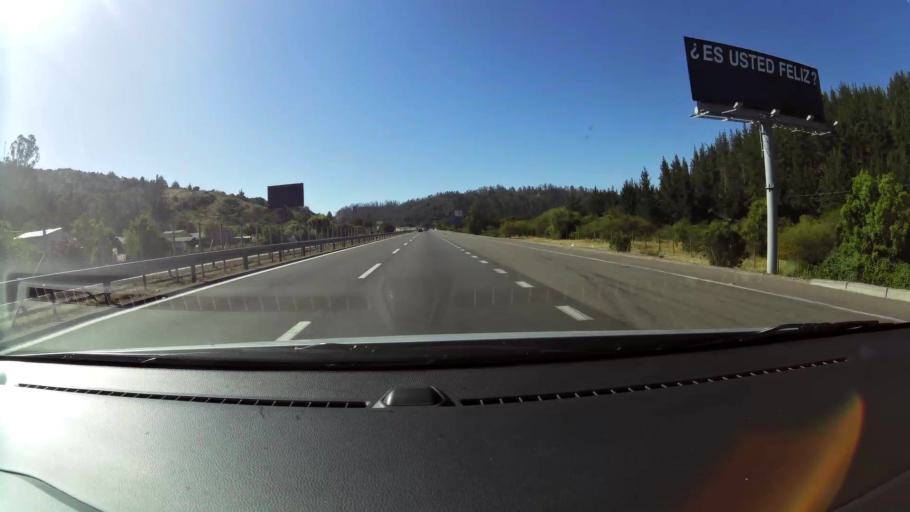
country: CL
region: Valparaiso
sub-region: Provincia de Marga Marga
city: Quilpue
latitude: -33.2193
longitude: -71.4718
